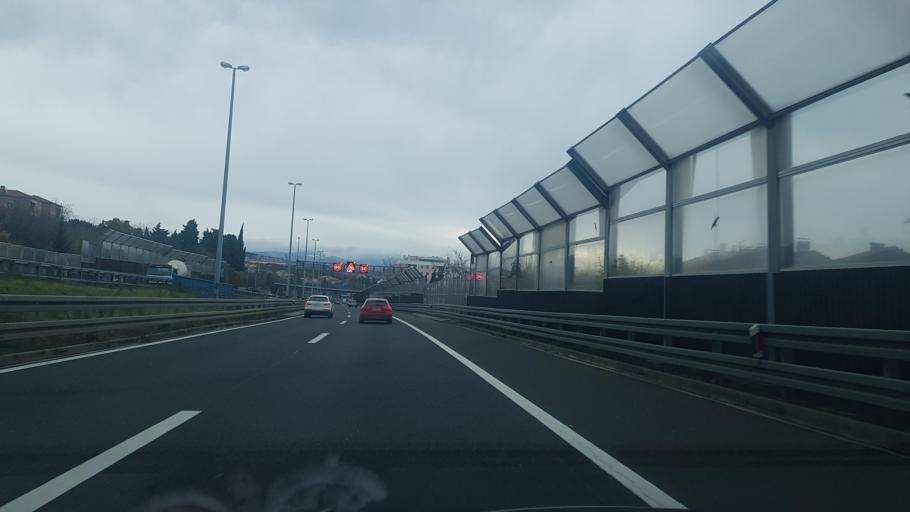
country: HR
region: Primorsko-Goranska
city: Rijeka
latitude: 45.3309
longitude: 14.4059
